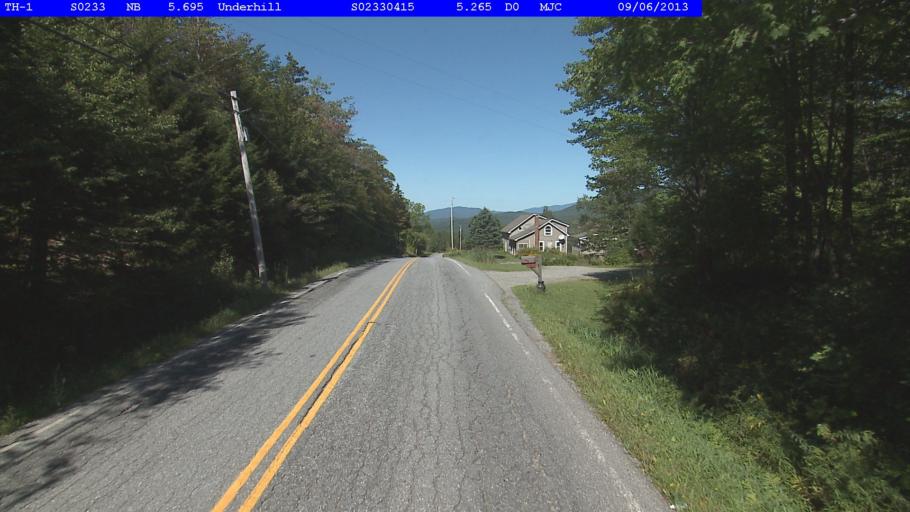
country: US
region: Vermont
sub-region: Chittenden County
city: Jericho
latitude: 44.5411
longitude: -72.8697
